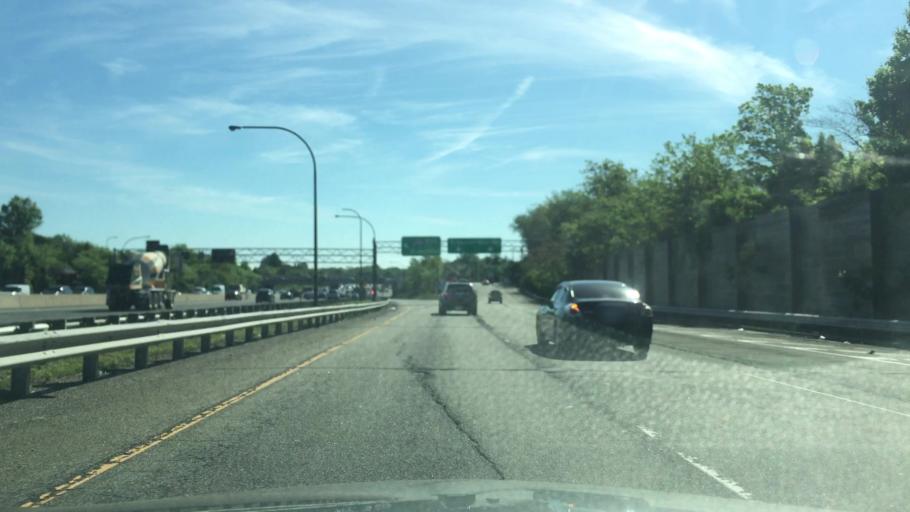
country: US
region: New York
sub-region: Nassau County
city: Syosset
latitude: 40.7960
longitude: -73.5071
